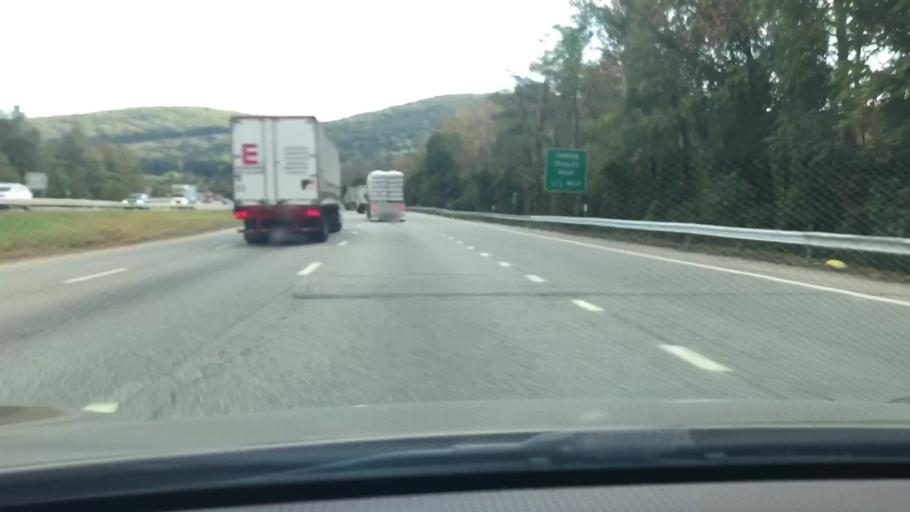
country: US
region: New York
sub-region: Rockland County
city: Sloatsburg
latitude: 41.1501
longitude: -74.1891
